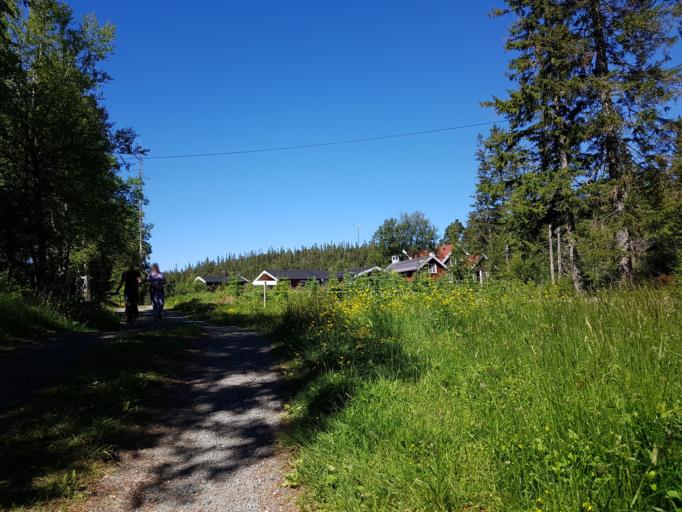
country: NO
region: Sor-Trondelag
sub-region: Skaun
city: Borsa
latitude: 63.4317
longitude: 10.1873
